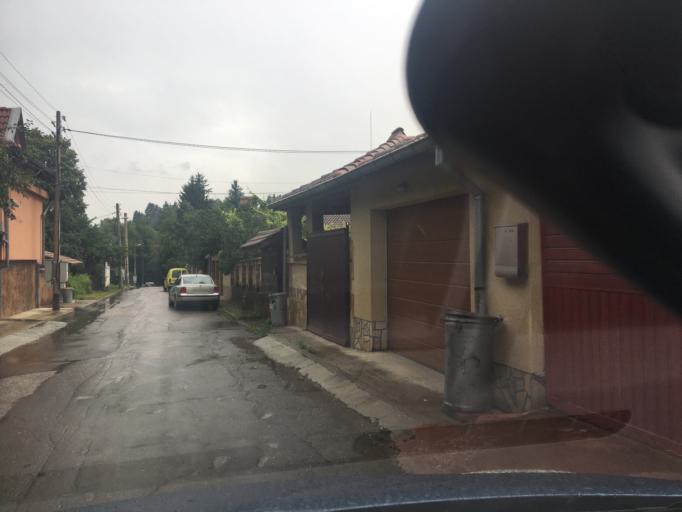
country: BG
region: Sofia-Capital
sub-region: Stolichna Obshtina
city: Sofia
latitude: 42.5853
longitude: 23.3525
